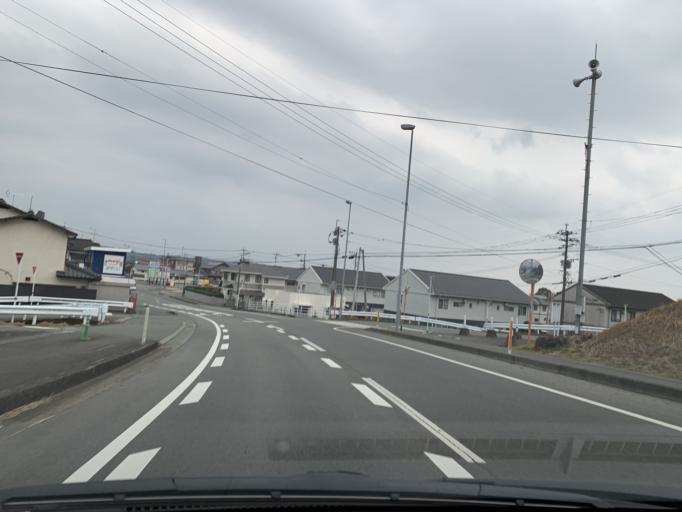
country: JP
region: Kumamoto
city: Ozu
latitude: 32.8814
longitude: 130.8771
